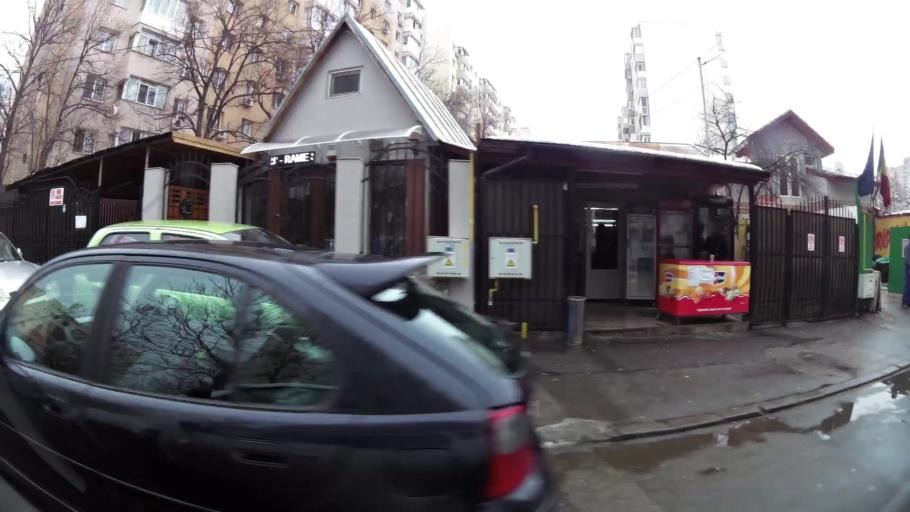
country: RO
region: Ilfov
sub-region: Comuna Popesti-Leordeni
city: Popesti-Leordeni
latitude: 44.4138
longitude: 26.1687
